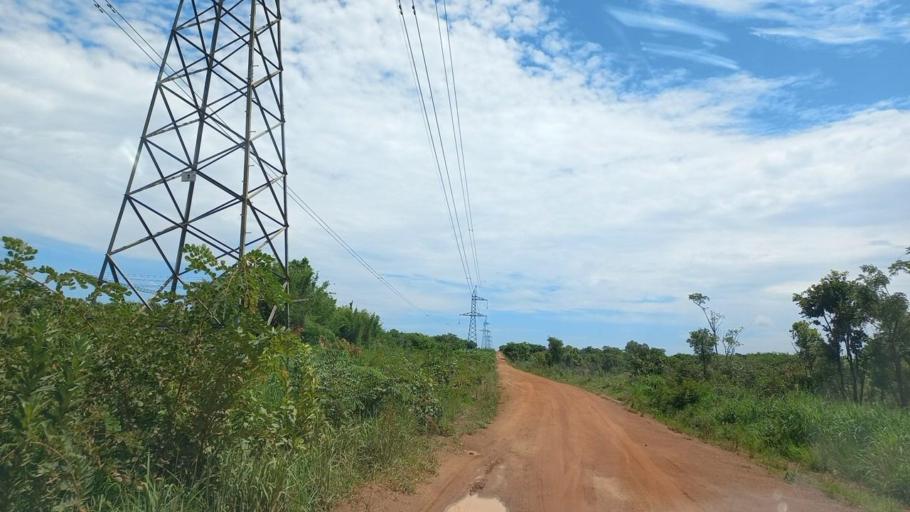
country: ZM
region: Copperbelt
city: Kitwe
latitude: -12.8104
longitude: 28.3598
